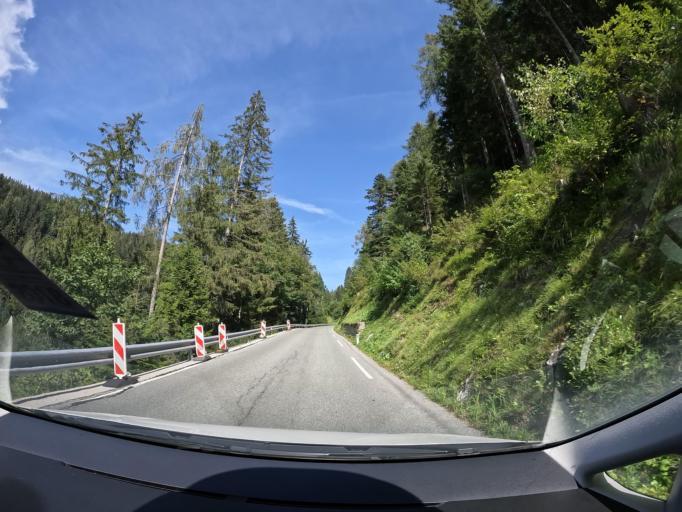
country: AT
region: Carinthia
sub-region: Politischer Bezirk Villach Land
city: Sankt Jakob
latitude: 46.5409
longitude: 14.0860
